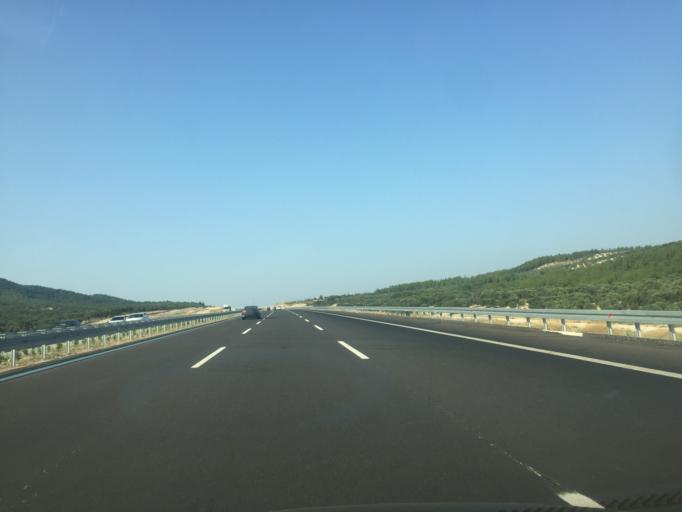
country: TR
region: Manisa
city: Zeytinliova
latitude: 38.9961
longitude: 27.7370
